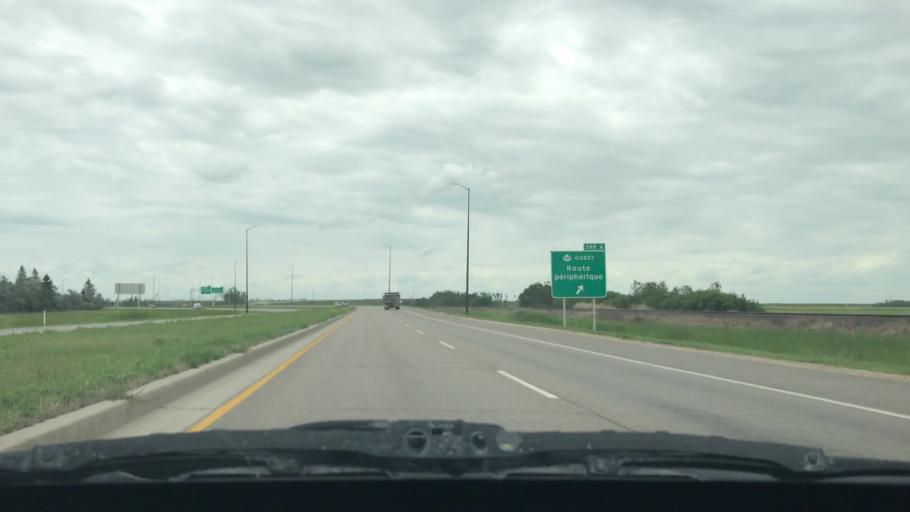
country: CA
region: Manitoba
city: Winnipeg
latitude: 49.8376
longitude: -96.9782
